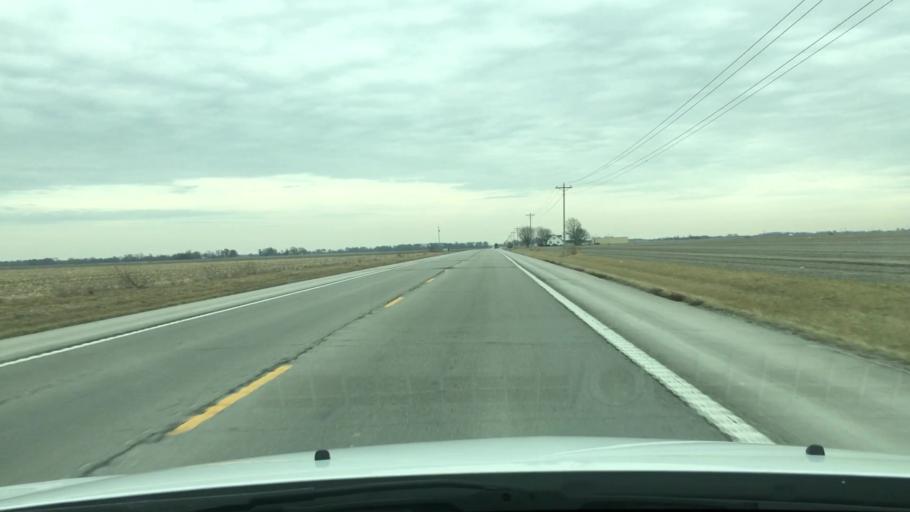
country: US
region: Missouri
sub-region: Audrain County
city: Mexico
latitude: 39.1639
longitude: -91.7851
